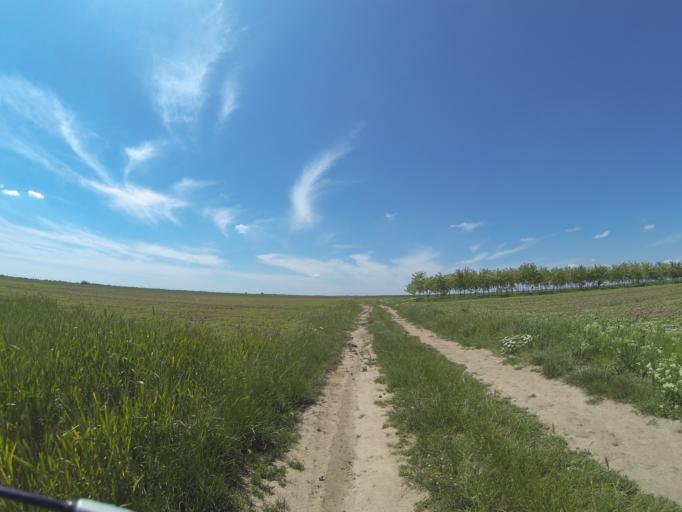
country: RO
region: Dolj
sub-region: Comuna Leu
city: Leu
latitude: 44.2203
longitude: 24.0089
